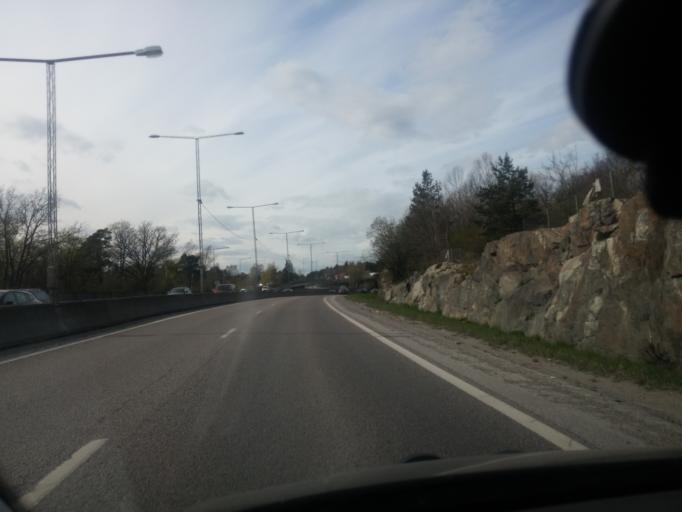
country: SE
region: Stockholm
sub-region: Stockholms Kommun
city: Kista
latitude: 59.3730
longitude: 17.9302
